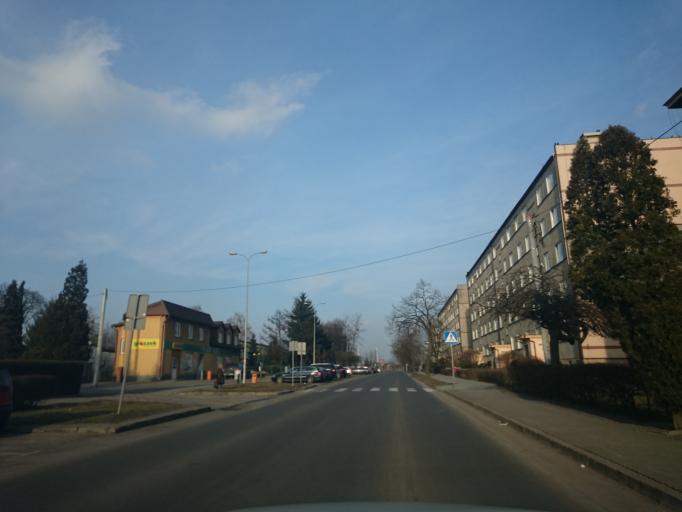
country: PL
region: Kujawsko-Pomorskie
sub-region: Powiat rypinski
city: Rypin
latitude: 53.0668
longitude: 19.4217
